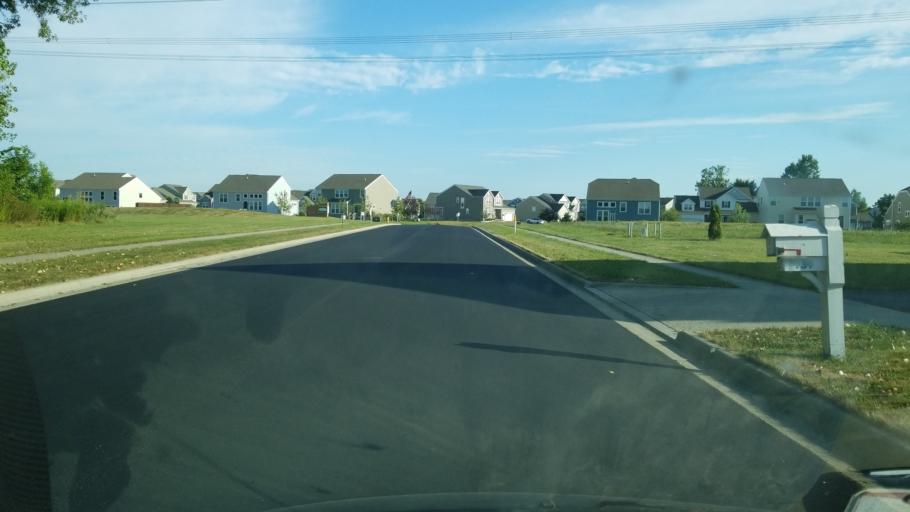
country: US
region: Ohio
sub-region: Delaware County
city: Lewis Center
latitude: 40.1811
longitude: -83.0027
